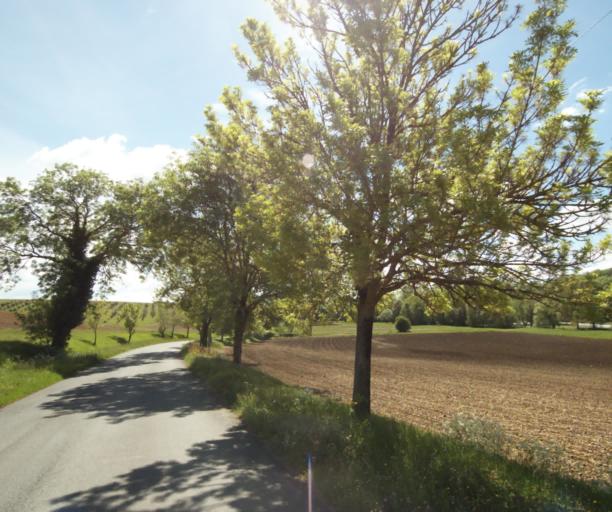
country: FR
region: Poitou-Charentes
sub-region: Departement de la Charente-Maritime
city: Chaniers
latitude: 45.7333
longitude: -0.5076
